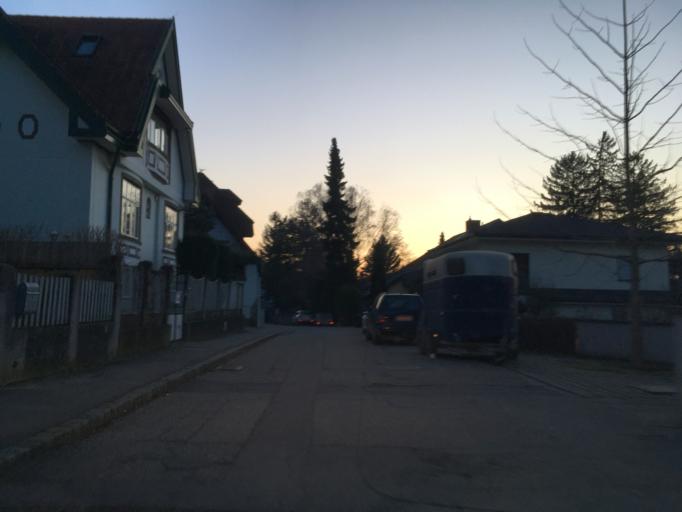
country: AT
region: Lower Austria
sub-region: Politischer Bezirk Tulln
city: Wordern
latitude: 48.3275
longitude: 16.2198
